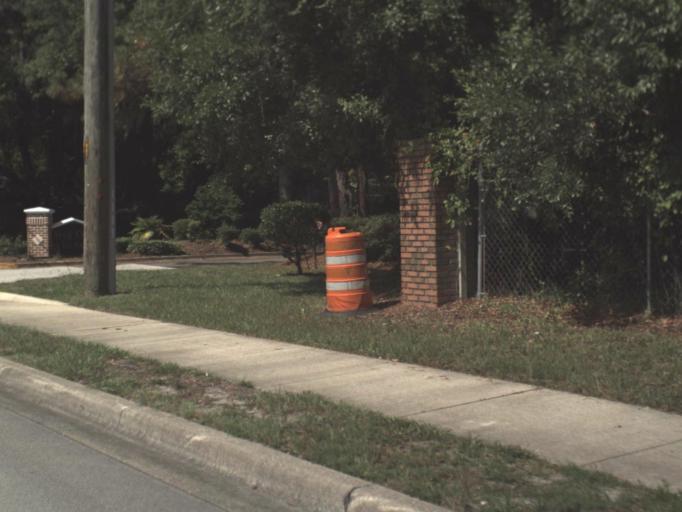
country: US
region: Florida
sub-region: Saint Johns County
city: Fruit Cove
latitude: 30.1157
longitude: -81.6260
